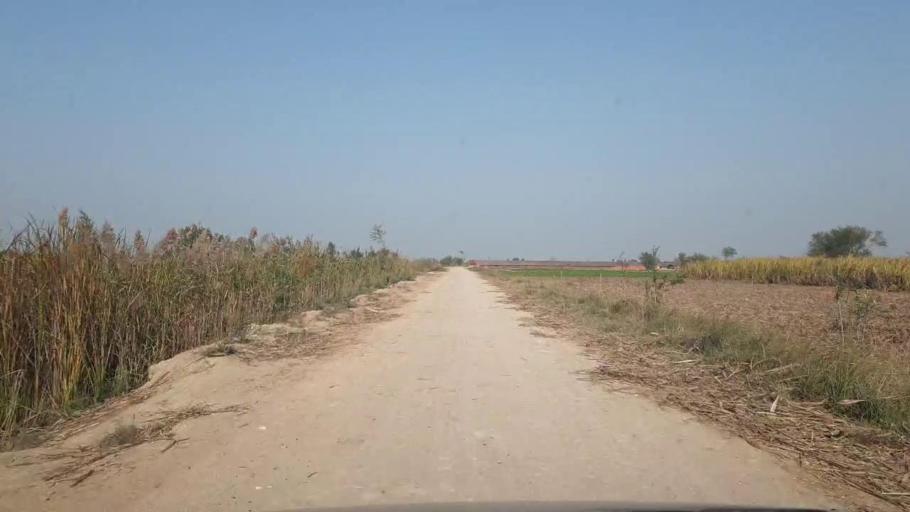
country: PK
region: Sindh
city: Bhit Shah
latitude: 25.8206
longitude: 68.5734
